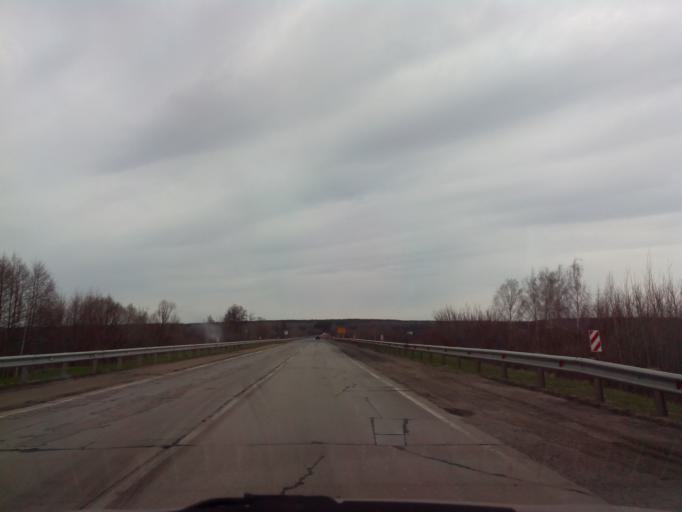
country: RU
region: Tambov
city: Znamenka
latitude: 52.5233
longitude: 41.3617
